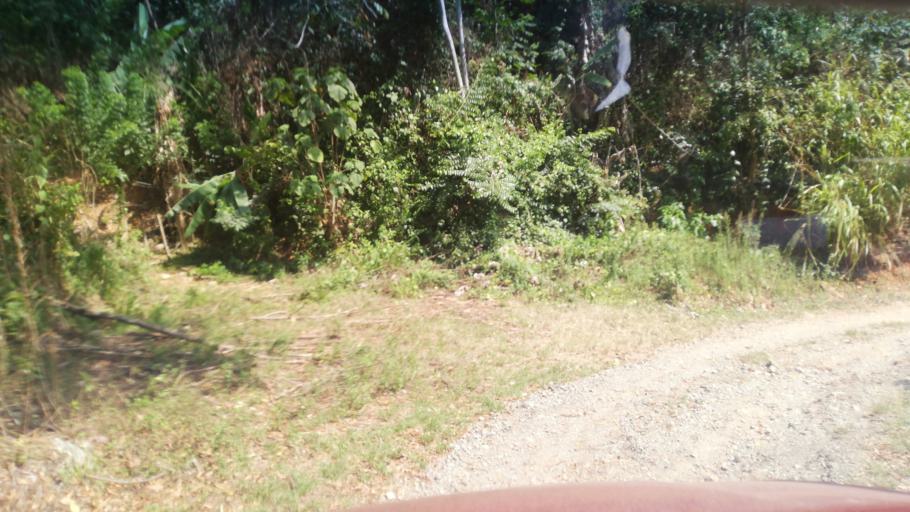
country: CO
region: Risaralda
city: Balboa
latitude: 4.9133
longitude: -75.9516
